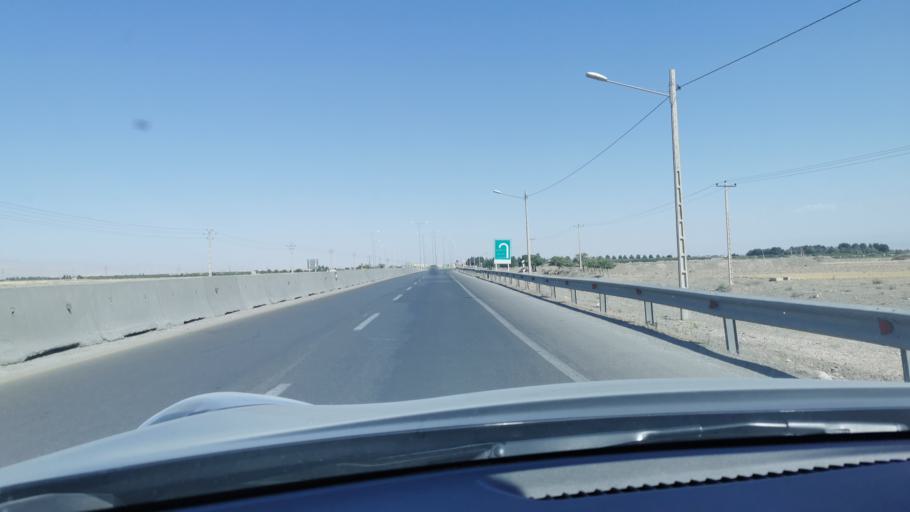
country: IR
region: Razavi Khorasan
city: Chenaran
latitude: 36.6207
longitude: 59.1551
